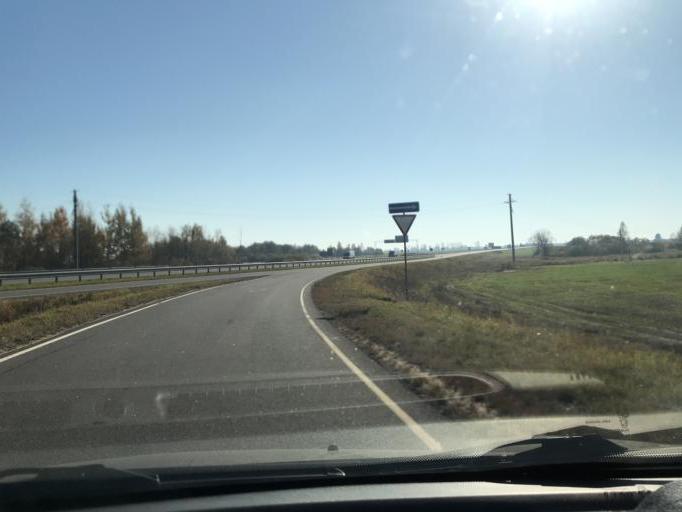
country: BY
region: Mogilev
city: Babruysk
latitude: 53.1820
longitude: 29.3567
